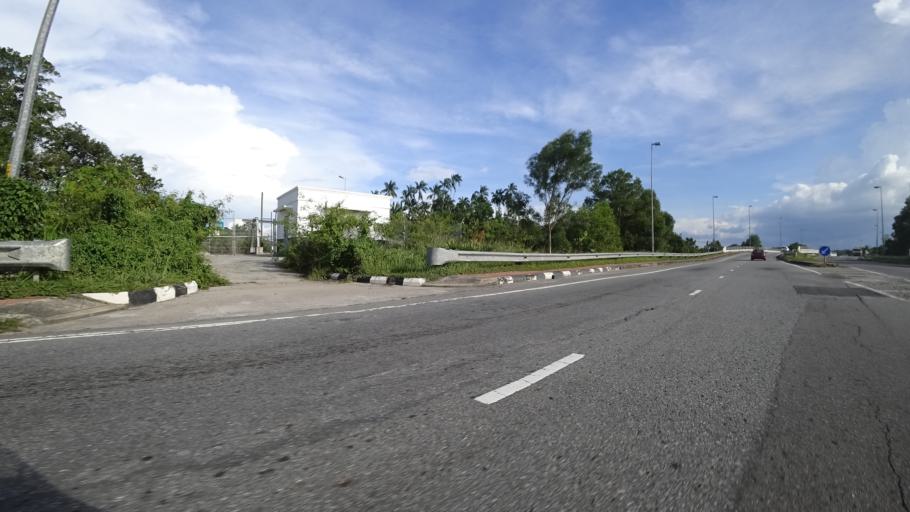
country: BN
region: Brunei and Muara
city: Bandar Seri Begawan
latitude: 4.8510
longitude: 114.8761
